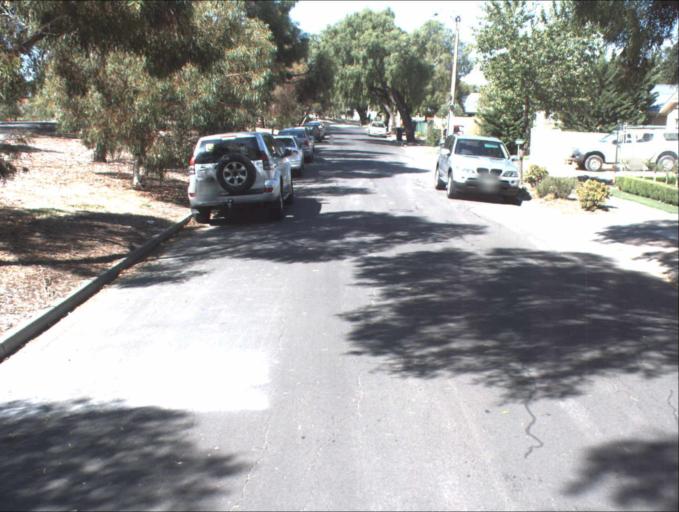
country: AU
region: South Australia
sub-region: Port Adelaide Enfield
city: Gilles Plains
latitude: -34.8590
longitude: 138.6484
